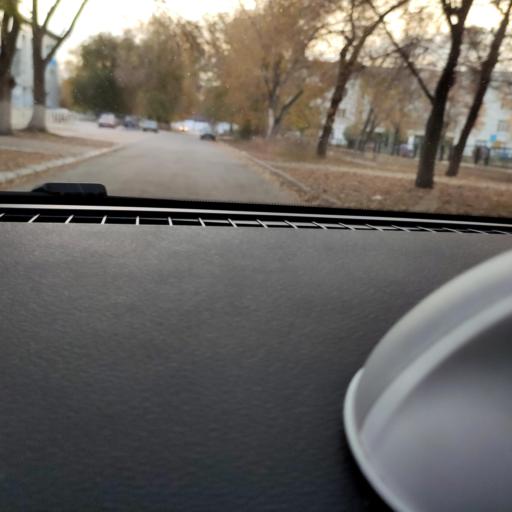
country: RU
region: Samara
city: Petra-Dubrava
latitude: 53.2375
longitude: 50.2705
